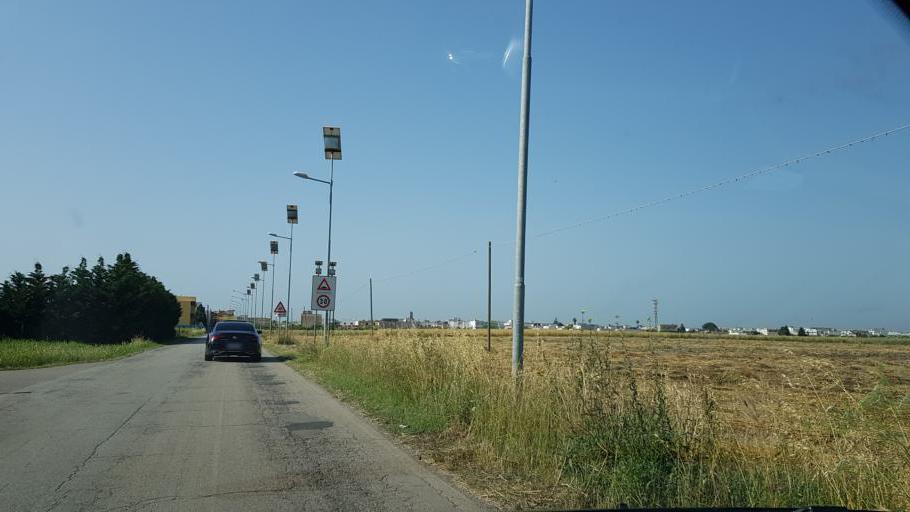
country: IT
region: Apulia
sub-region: Provincia di Brindisi
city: San Pancrazio Salentino
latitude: 40.4273
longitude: 17.8407
